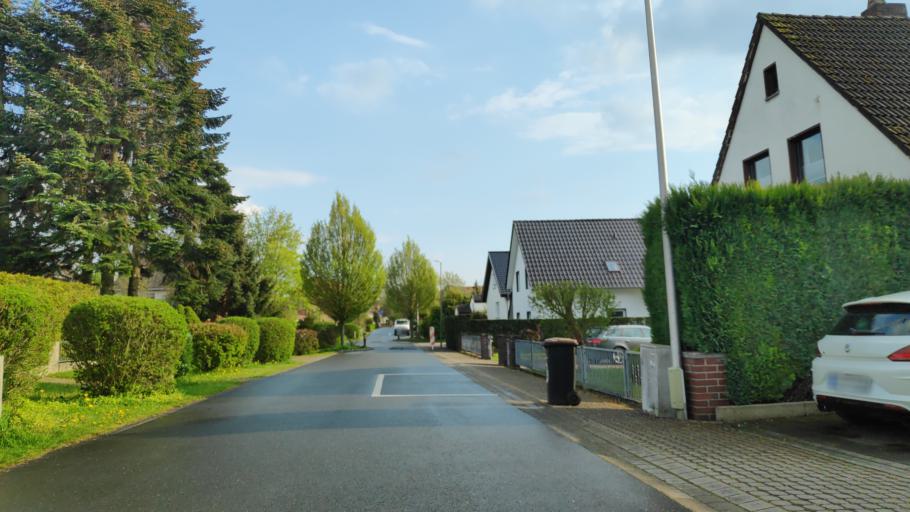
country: DE
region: North Rhine-Westphalia
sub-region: Regierungsbezirk Detmold
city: Minden
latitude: 52.2893
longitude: 8.9531
